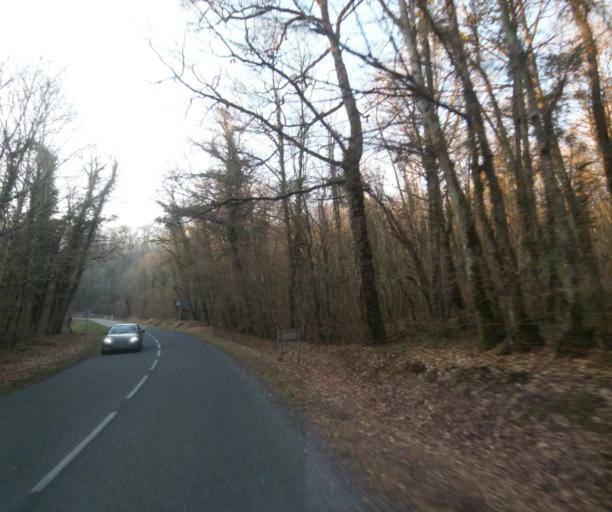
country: FR
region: Champagne-Ardenne
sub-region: Departement de la Haute-Marne
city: Bienville
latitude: 48.6128
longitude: 5.0606
